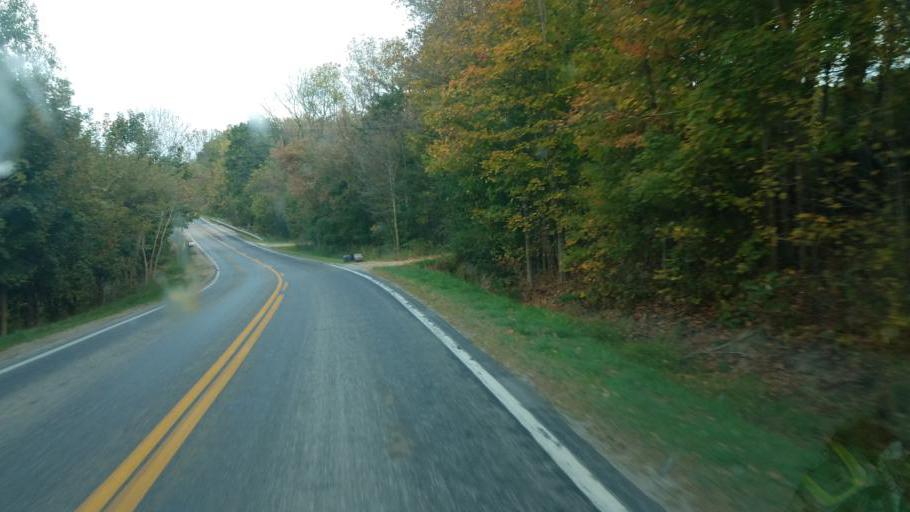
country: US
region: Ohio
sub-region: Ashland County
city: Loudonville
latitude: 40.7231
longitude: -82.1864
